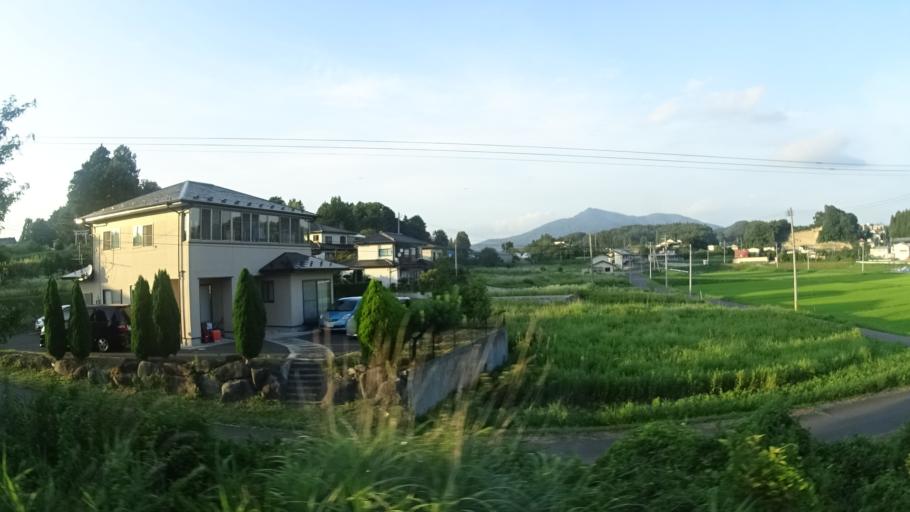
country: JP
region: Fukushima
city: Funehikimachi-funehiki
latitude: 37.4465
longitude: 140.5680
